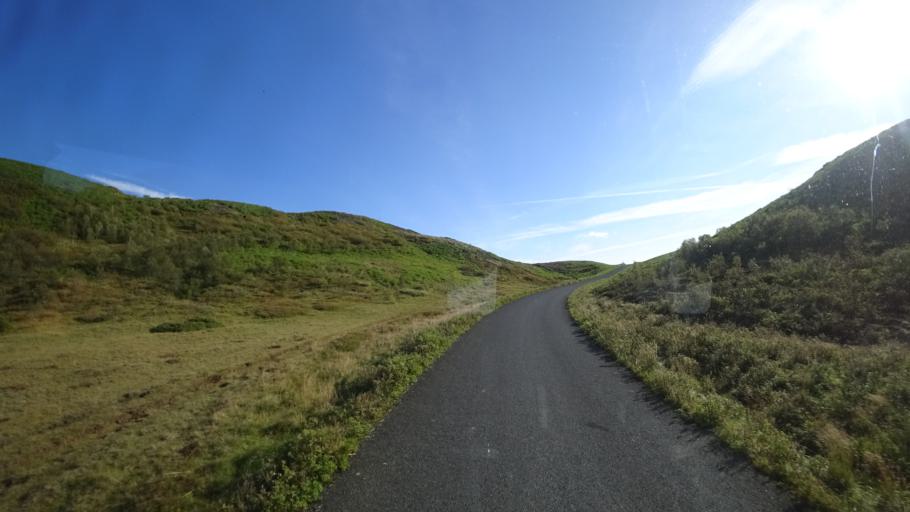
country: IS
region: South
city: Hveragerdi
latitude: 64.1371
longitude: -21.2507
